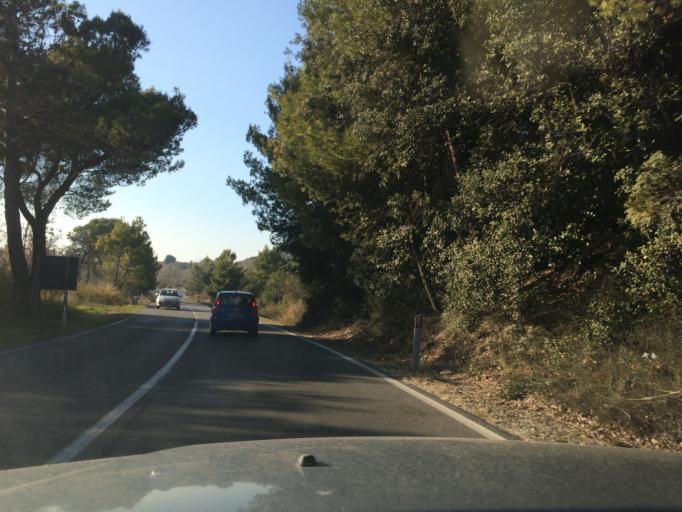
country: IT
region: Umbria
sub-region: Provincia di Terni
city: Fornole
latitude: 42.5395
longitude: 12.4762
